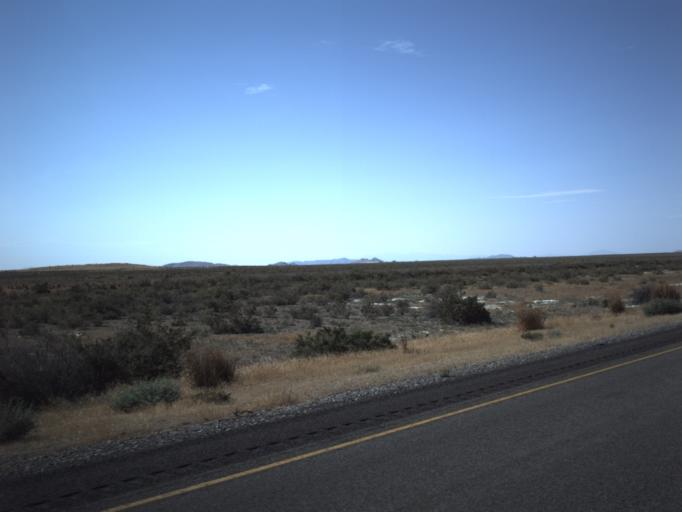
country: US
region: Utah
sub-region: Tooele County
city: Grantsville
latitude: 40.7448
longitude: -113.0690
